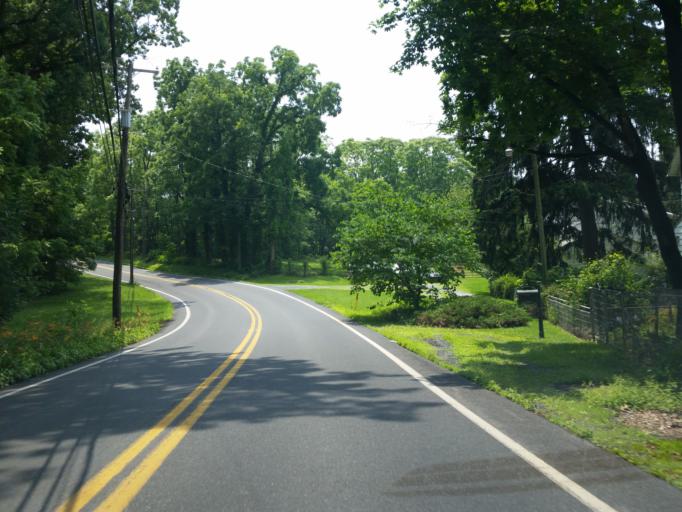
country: US
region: Pennsylvania
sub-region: Lebanon County
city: Campbelltown
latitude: 40.2639
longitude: -76.5899
